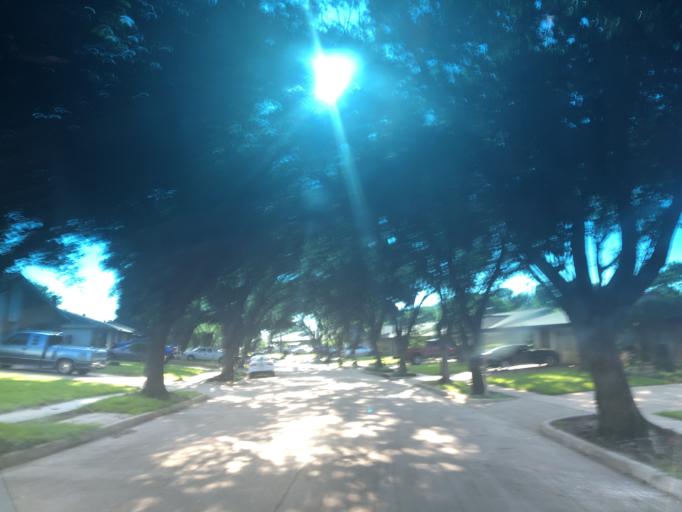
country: US
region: Texas
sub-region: Dallas County
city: Grand Prairie
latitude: 32.7026
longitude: -97.0020
